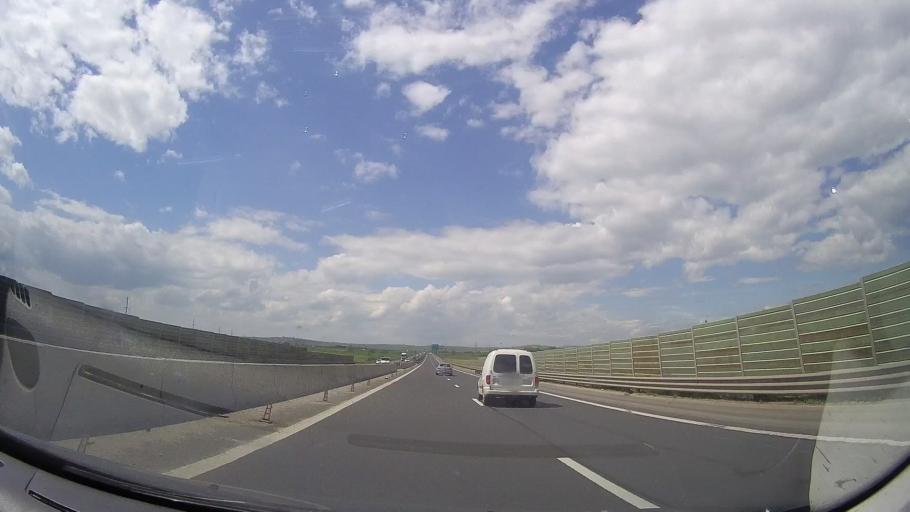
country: RO
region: Sibiu
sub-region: Municipiul Sibiu
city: Sibiu
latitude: 45.8103
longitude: 24.1725
